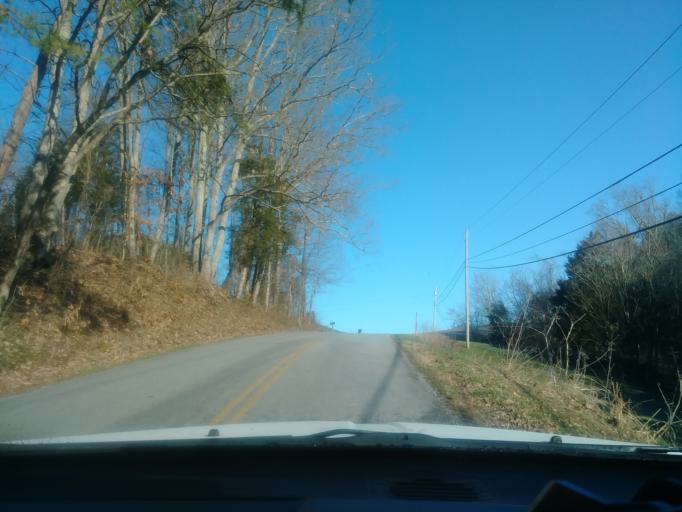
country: US
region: Tennessee
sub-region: Greene County
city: Mosheim
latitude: 36.1057
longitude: -82.9289
